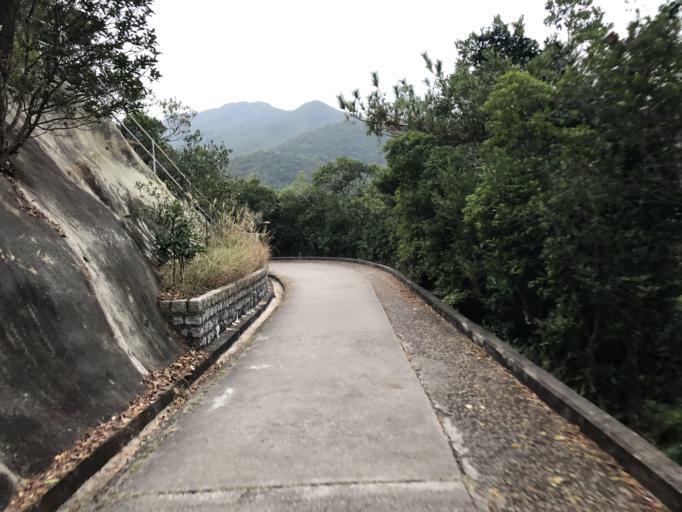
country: HK
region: Wanchai
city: Wan Chai
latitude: 22.2603
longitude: 114.2119
